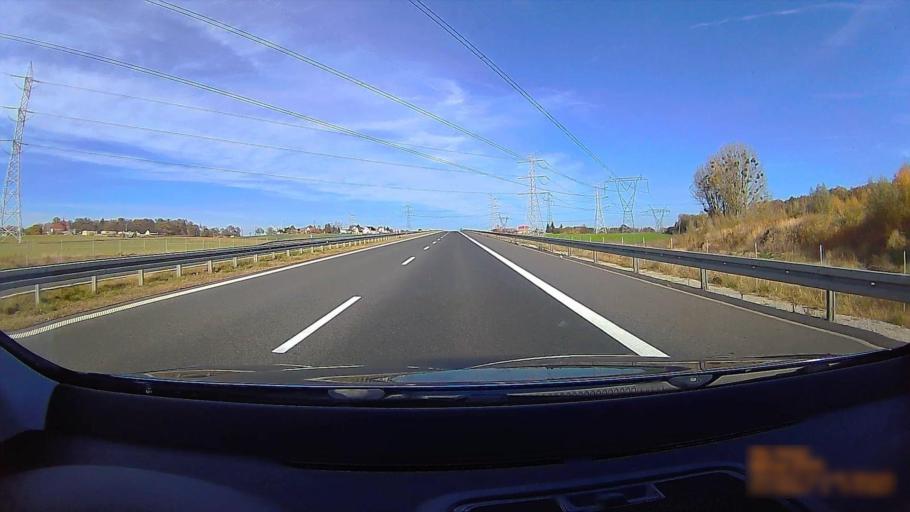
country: PL
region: Greater Poland Voivodeship
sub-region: Powiat ostrowski
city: Przygodzice
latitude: 51.6166
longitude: 17.8601
